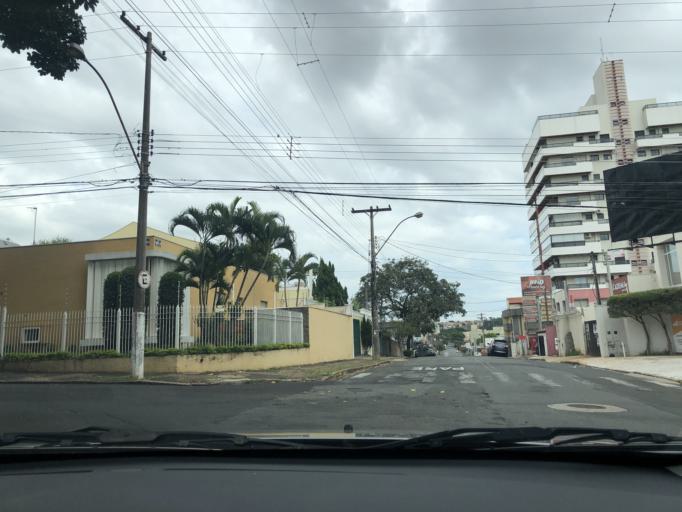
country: BR
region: Sao Paulo
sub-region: Americana
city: Americana
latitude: -22.7401
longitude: -47.3358
